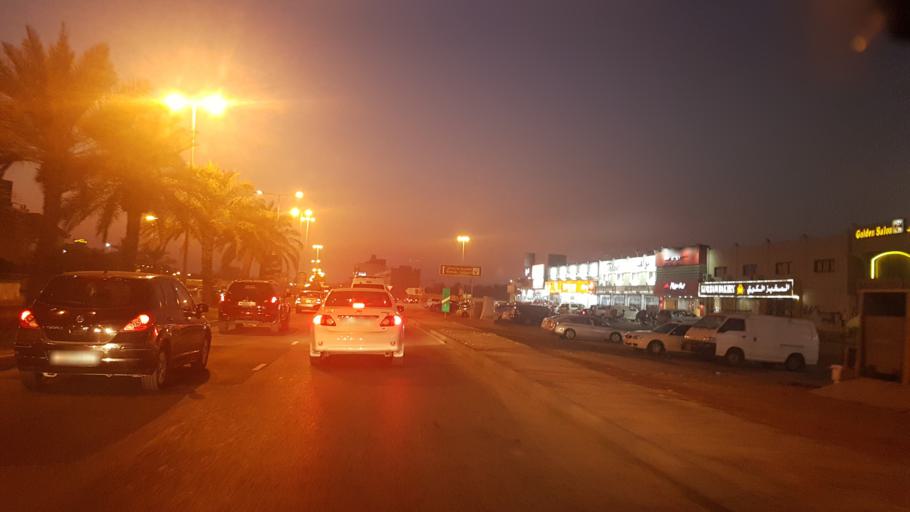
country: BH
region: Manama
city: Jidd Hafs
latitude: 26.2206
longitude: 50.5008
